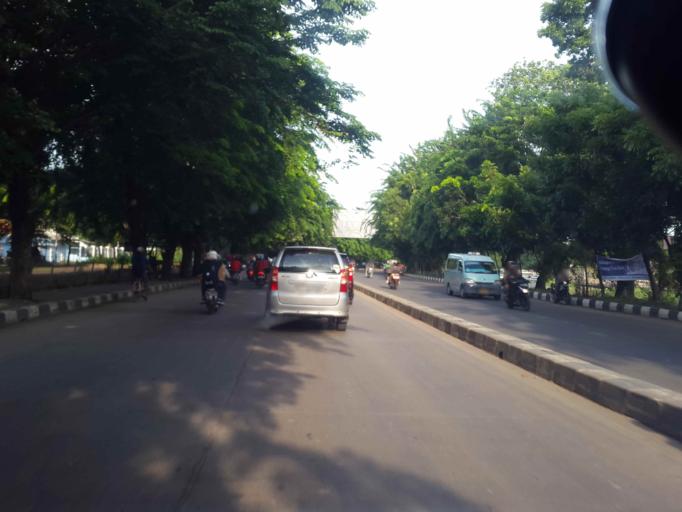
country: ID
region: West Java
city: Bekasi
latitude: -6.2480
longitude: 106.9745
